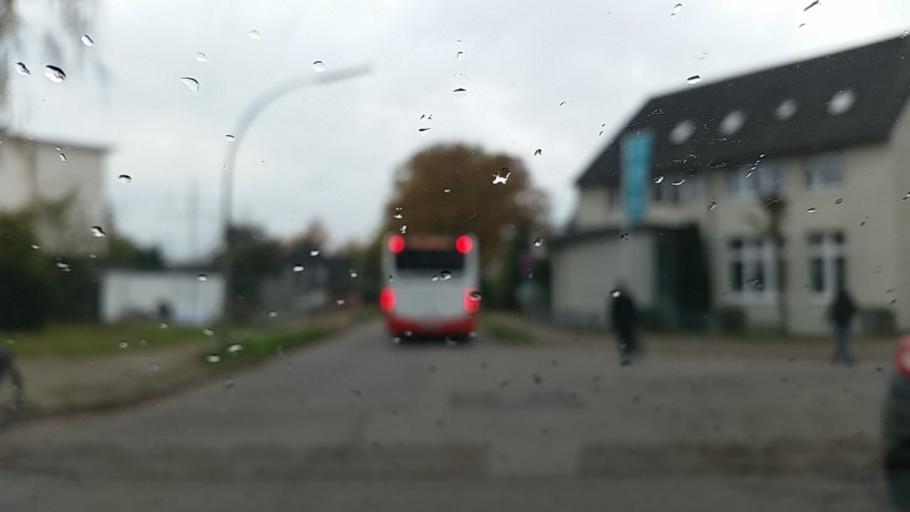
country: DE
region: Hamburg
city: Wandsbek
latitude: 53.5546
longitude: 10.1003
